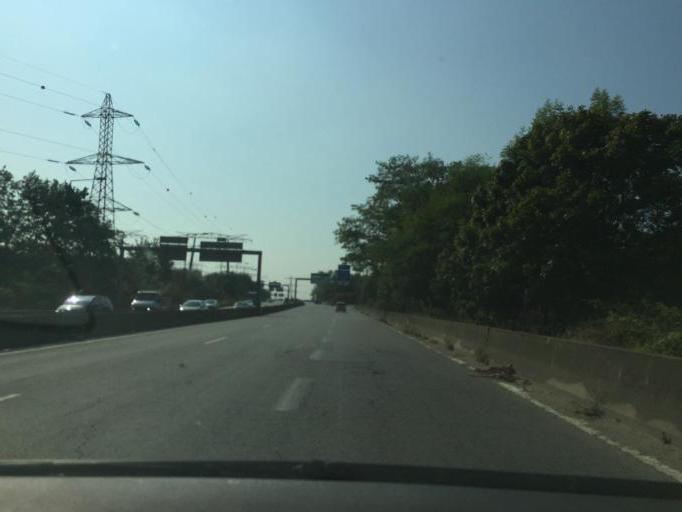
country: FR
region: Ile-de-France
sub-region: Departement de l'Essonne
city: Champlan
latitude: 48.7193
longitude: 2.2704
